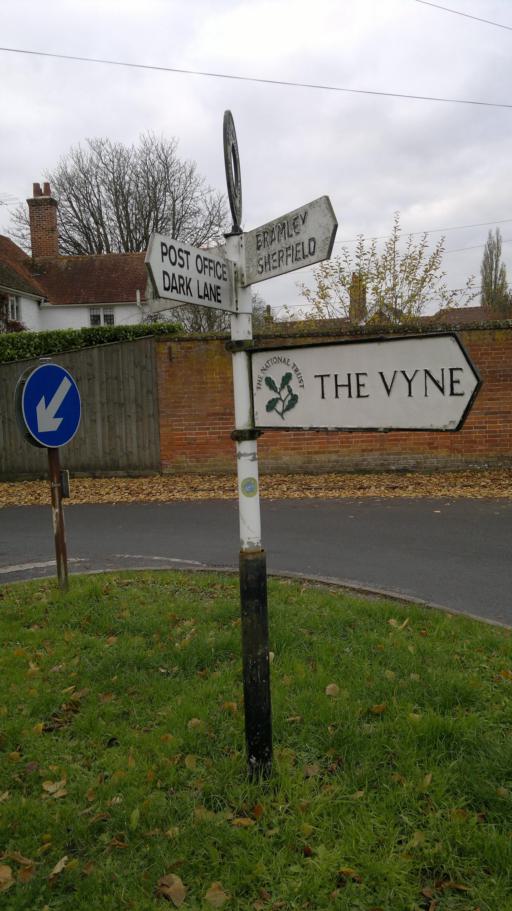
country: GB
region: England
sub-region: Hampshire
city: Basingstoke
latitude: 51.2952
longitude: -1.1046
